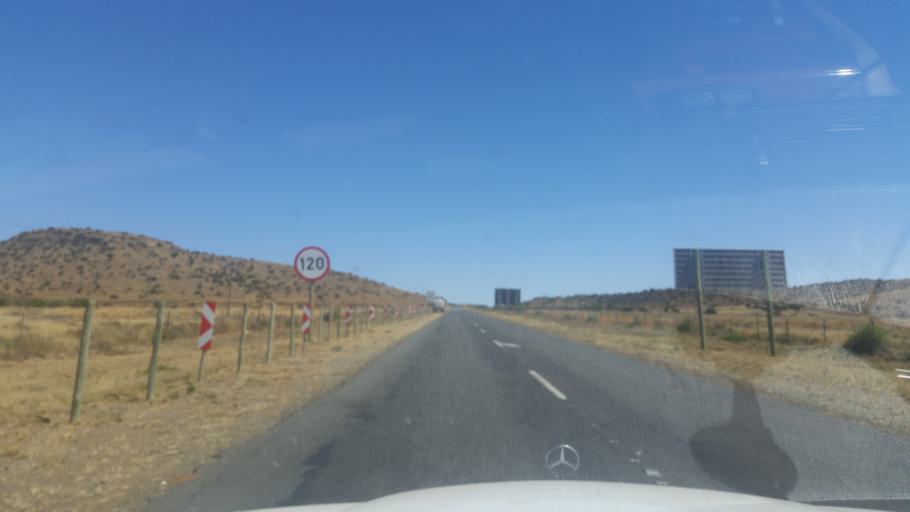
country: ZA
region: Eastern Cape
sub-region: Joe Gqabi District Municipality
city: Burgersdorp
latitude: -30.7784
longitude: 25.7573
